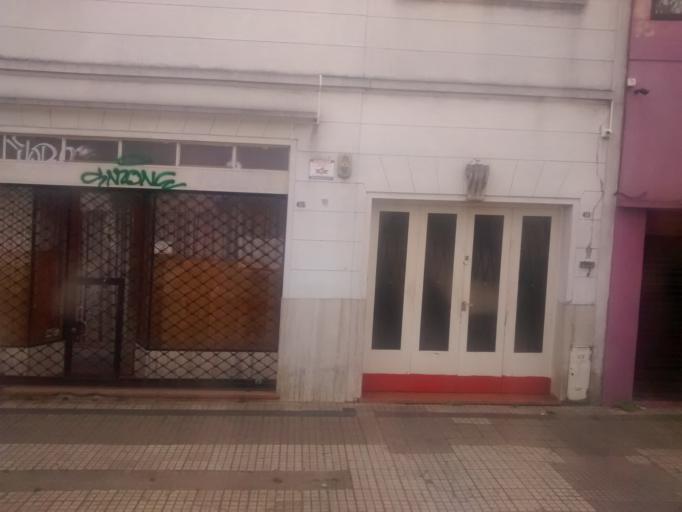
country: AR
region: Buenos Aires
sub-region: Partido de La Plata
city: La Plata
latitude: -34.9251
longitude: -57.9276
